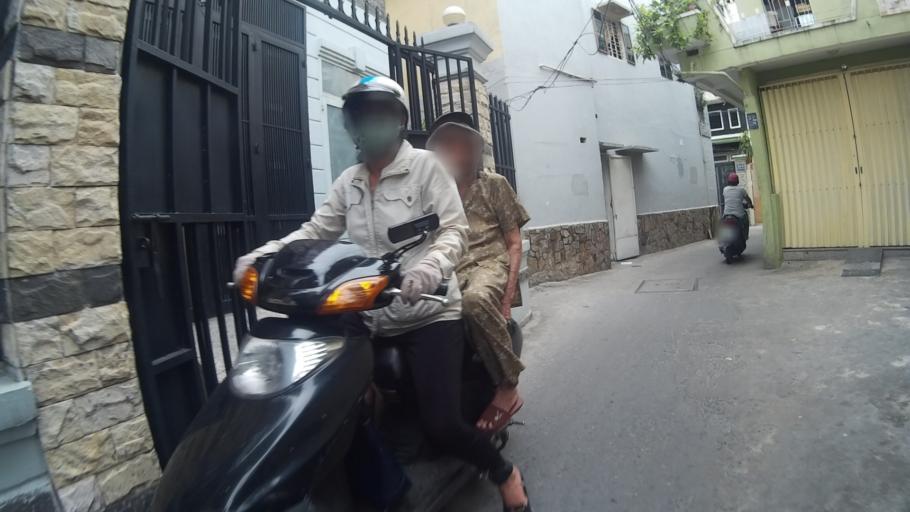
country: VN
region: Ho Chi Minh City
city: Quan Phu Nhuan
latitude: 10.7981
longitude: 106.6822
